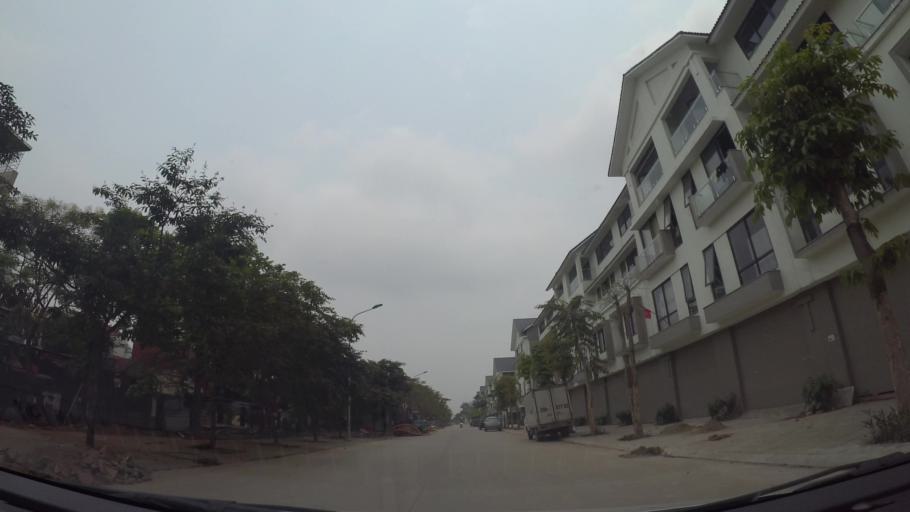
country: VN
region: Ha Noi
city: Ha Dong
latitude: 20.9875
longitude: 105.7413
